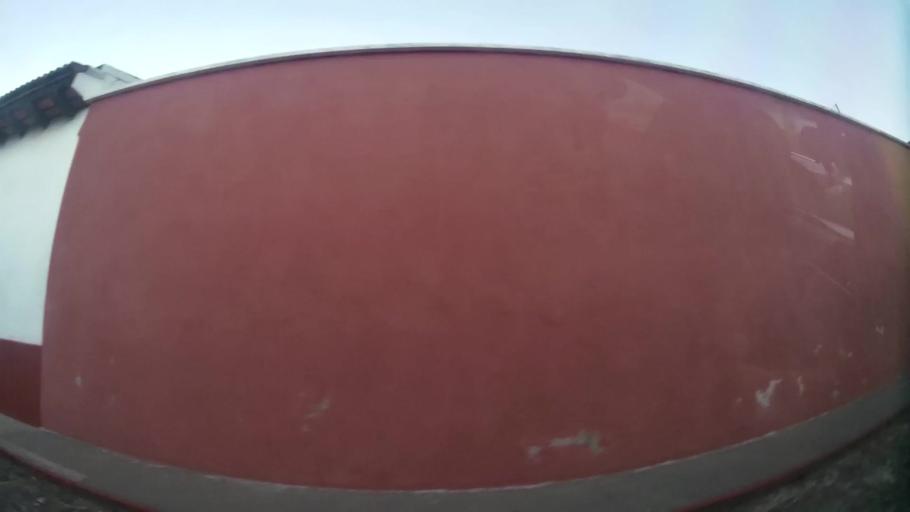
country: GT
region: Sacatepequez
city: Antigua Guatemala
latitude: 14.5556
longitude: -90.7311
